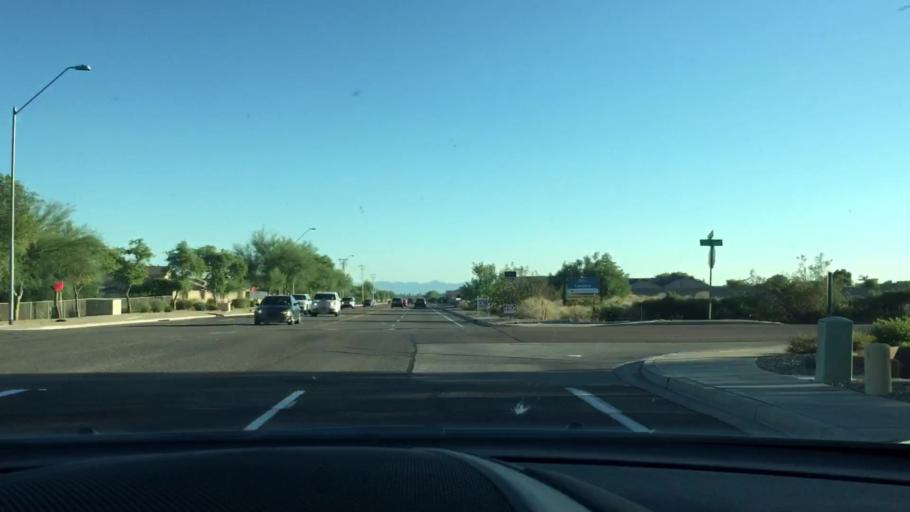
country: US
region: Arizona
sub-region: Maricopa County
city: Sun City
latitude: 33.7037
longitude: -112.2377
